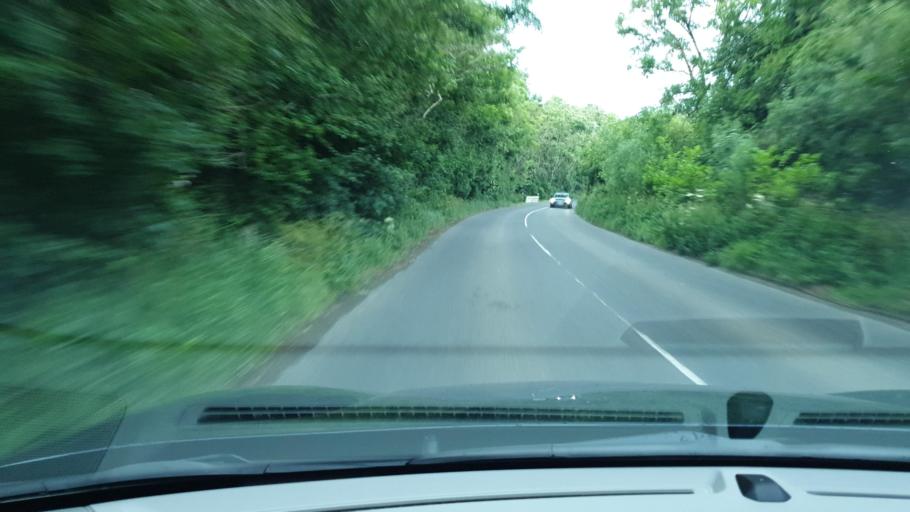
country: IE
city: Kentstown
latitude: 53.5929
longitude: -6.4999
